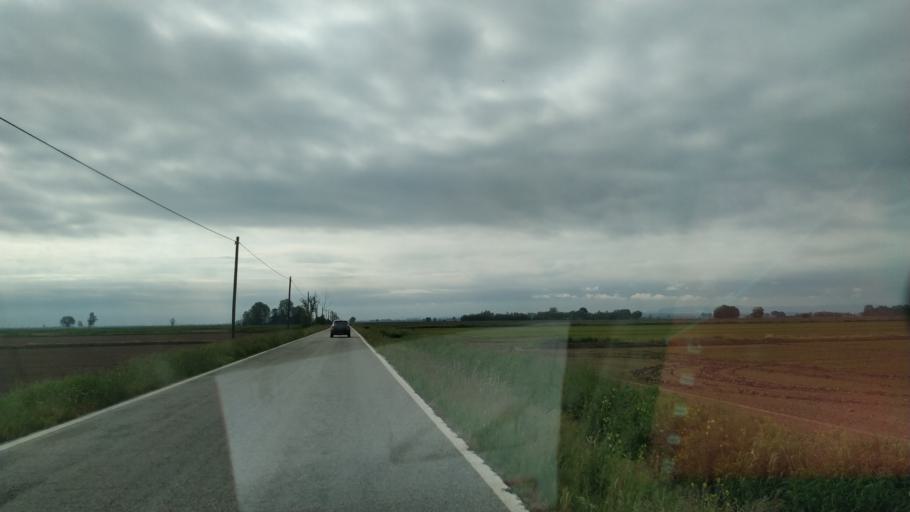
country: IT
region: Piedmont
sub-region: Provincia di Vercelli
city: Crova
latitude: 45.3053
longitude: 8.2082
